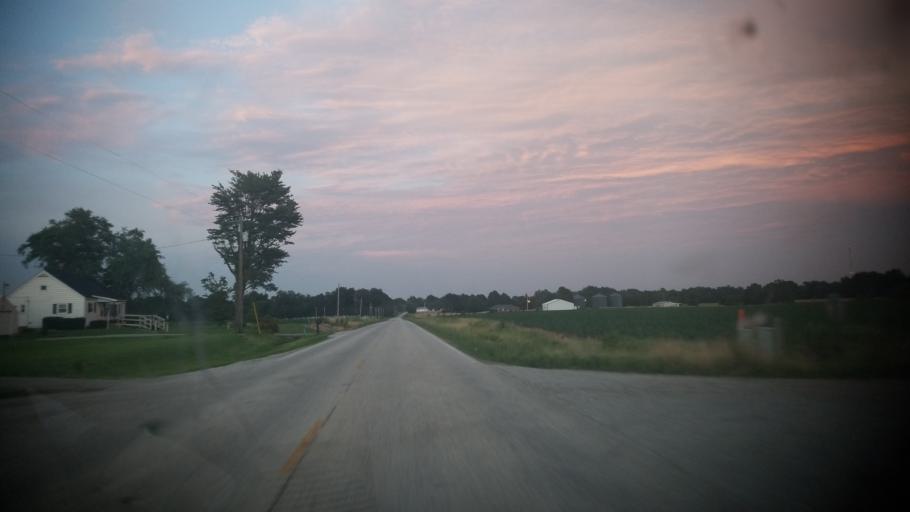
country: US
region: Illinois
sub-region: Clay County
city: Flora
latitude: 38.5160
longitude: -88.4535
